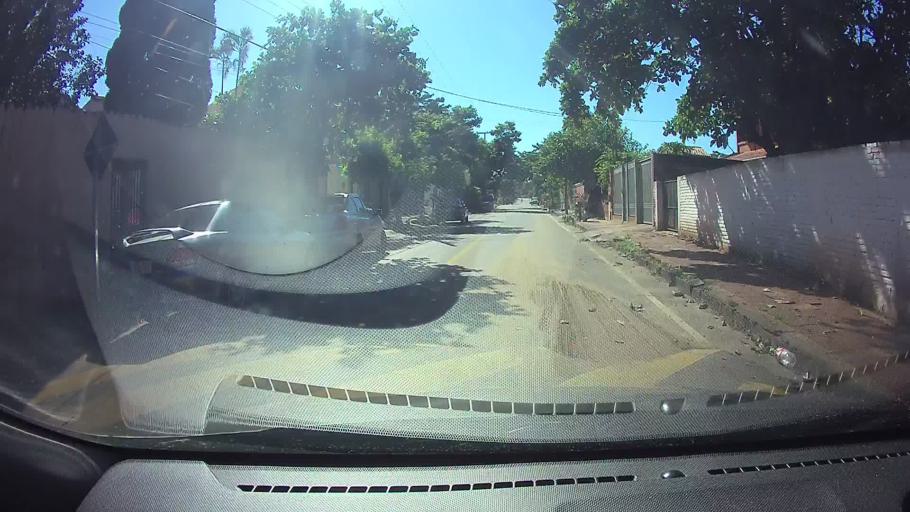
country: PY
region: Central
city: Fernando de la Mora
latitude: -25.2773
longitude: -57.5126
